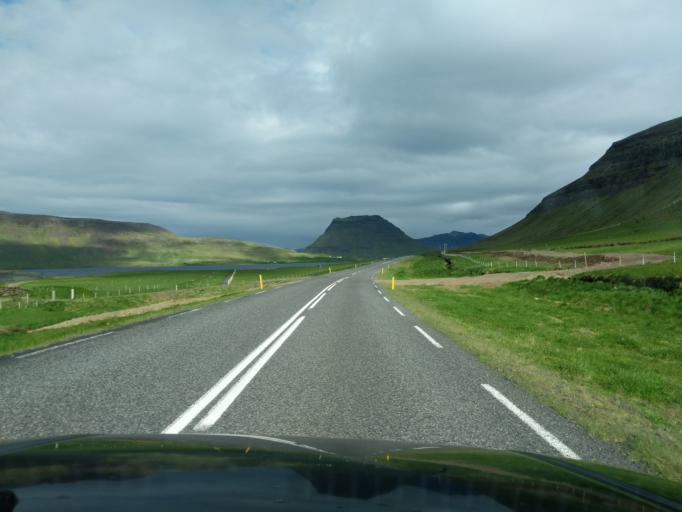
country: IS
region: West
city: Olafsvik
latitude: 64.9468
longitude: -23.4234
